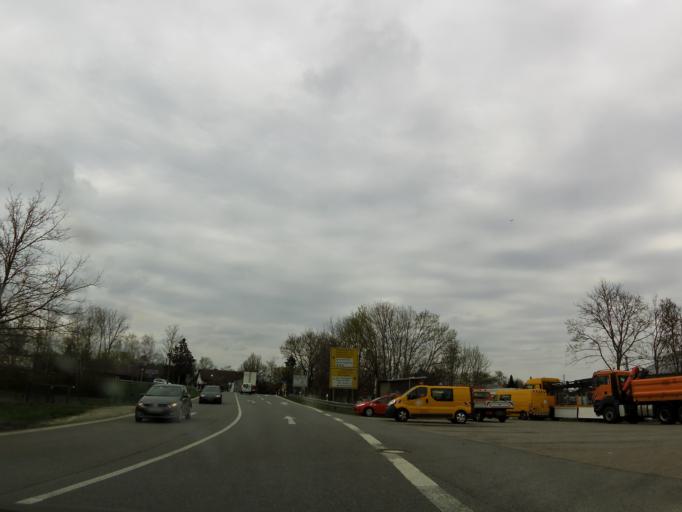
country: DE
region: Bavaria
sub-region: Upper Bavaria
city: Allershausen
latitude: 48.4282
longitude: 11.5909
